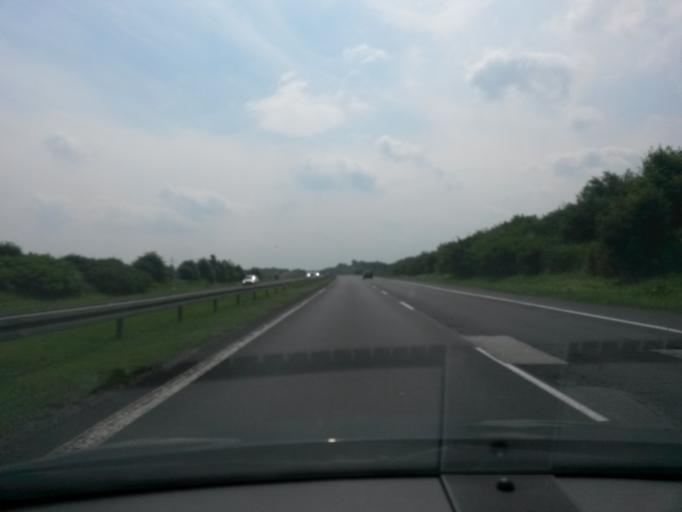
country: PL
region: Lodz Voivodeship
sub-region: Powiat radomszczanski
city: Kamiensk
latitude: 51.2013
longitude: 19.4777
